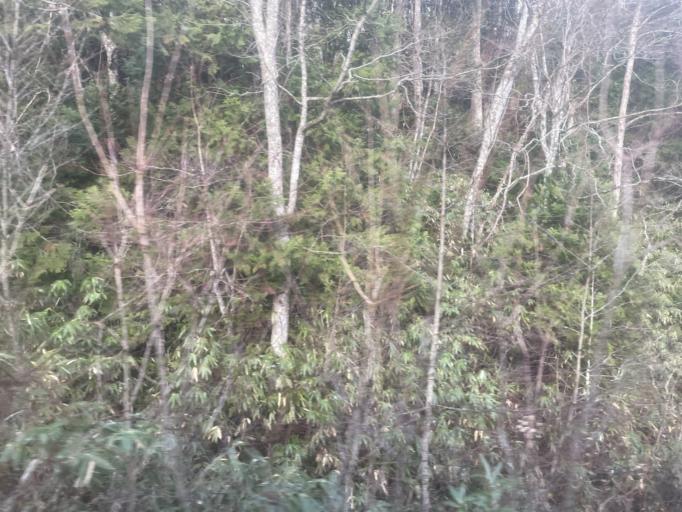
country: JP
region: Aomori
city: Goshogawara
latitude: 41.0781
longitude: 140.5326
